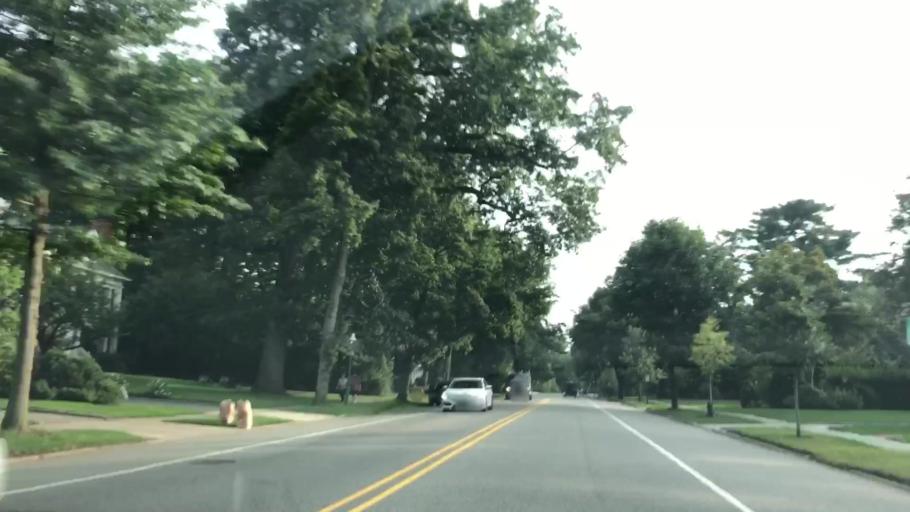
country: US
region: New Jersey
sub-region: Essex County
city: Glen Ridge
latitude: 40.8078
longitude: -74.2006
